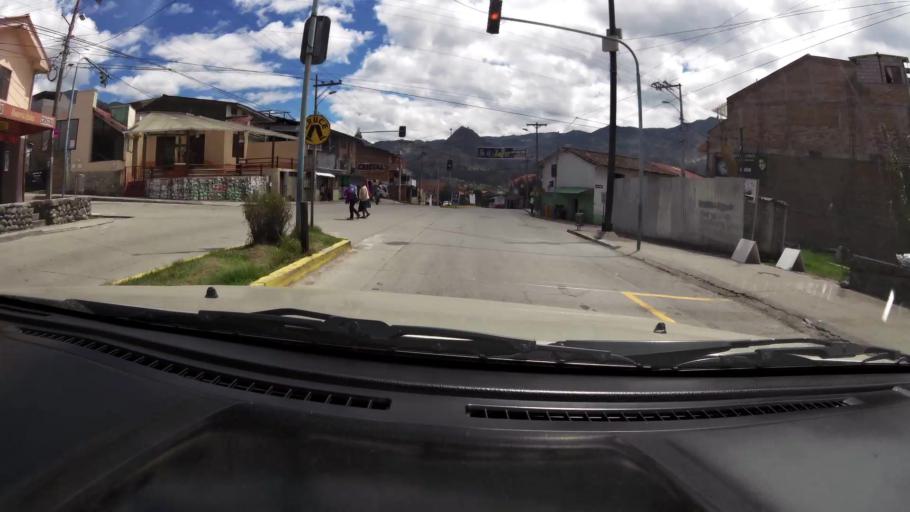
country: EC
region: Azuay
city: Cuenca
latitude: -3.1590
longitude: -79.1498
